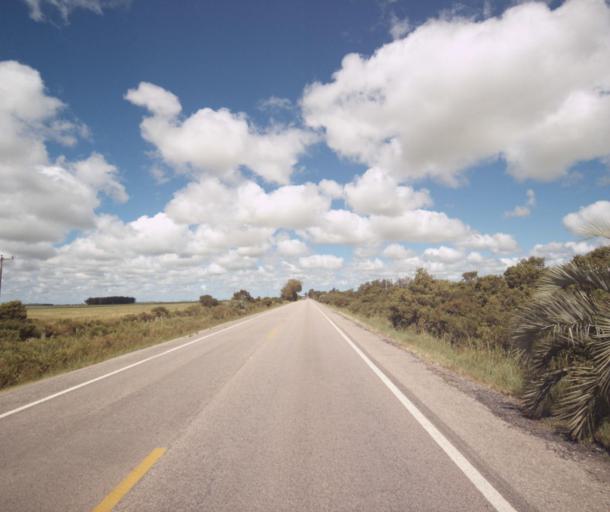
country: BR
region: Rio Grande do Sul
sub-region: Rio Grande
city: Rio Grande
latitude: -32.1791
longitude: -52.4214
